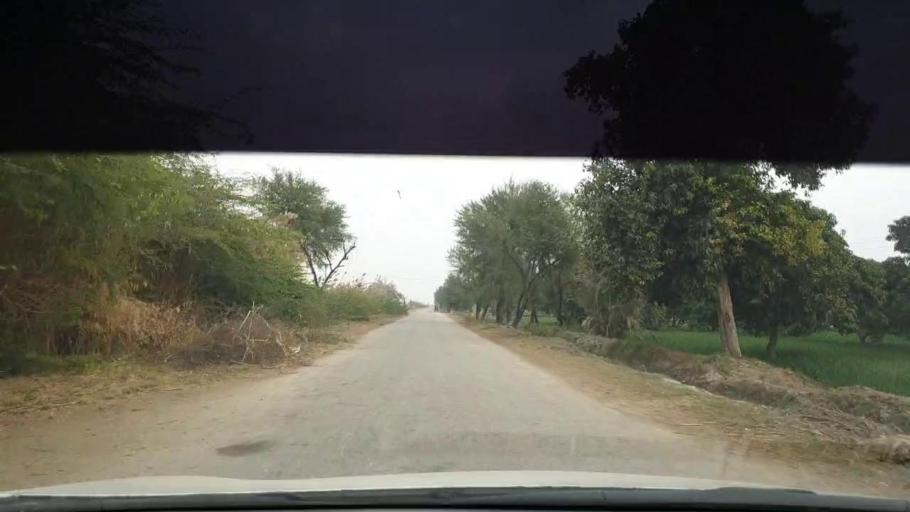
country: PK
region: Sindh
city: Berani
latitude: 25.7761
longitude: 68.8687
